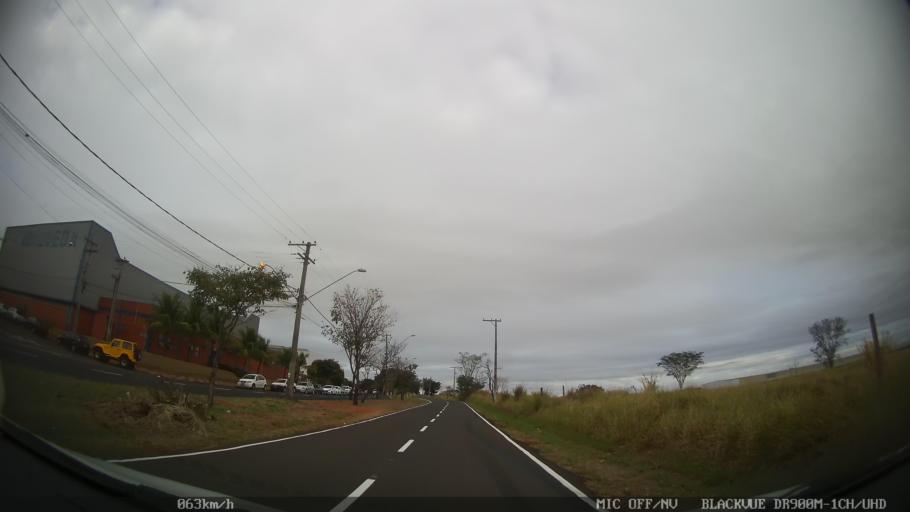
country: BR
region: Sao Paulo
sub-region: Sao Jose Do Rio Preto
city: Sao Jose do Rio Preto
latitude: -20.8267
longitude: -49.4235
